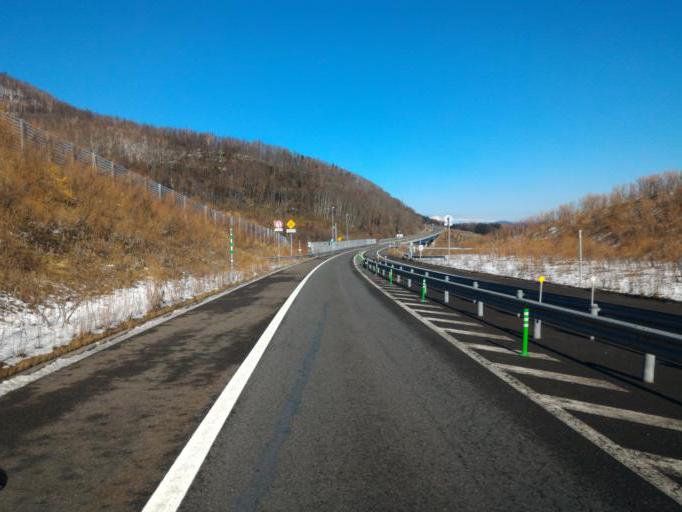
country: JP
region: Hokkaido
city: Otofuke
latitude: 43.0422
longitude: 142.7836
